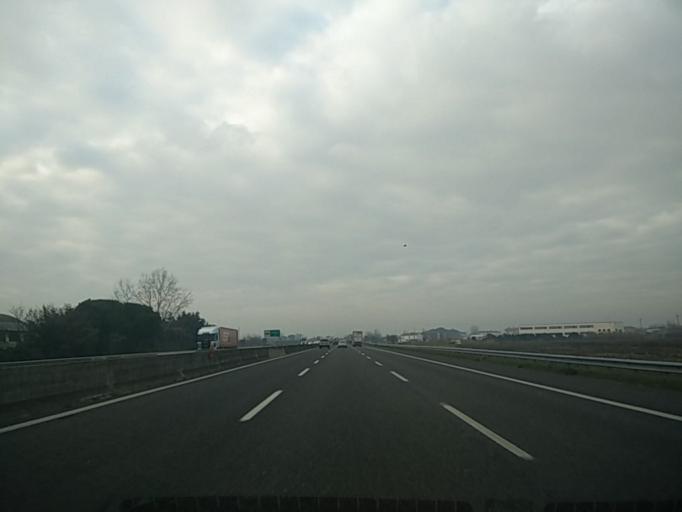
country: IT
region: Emilia-Romagna
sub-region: Forli-Cesena
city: Gatteo-Sant'Angelo
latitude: 44.1247
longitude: 12.3837
